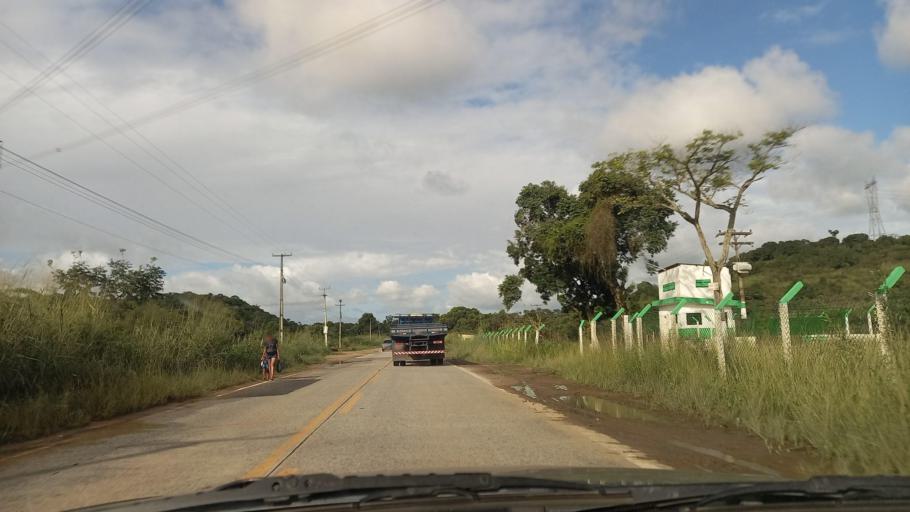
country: BR
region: Pernambuco
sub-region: Palmares
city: Palmares
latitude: -8.6912
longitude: -35.6152
